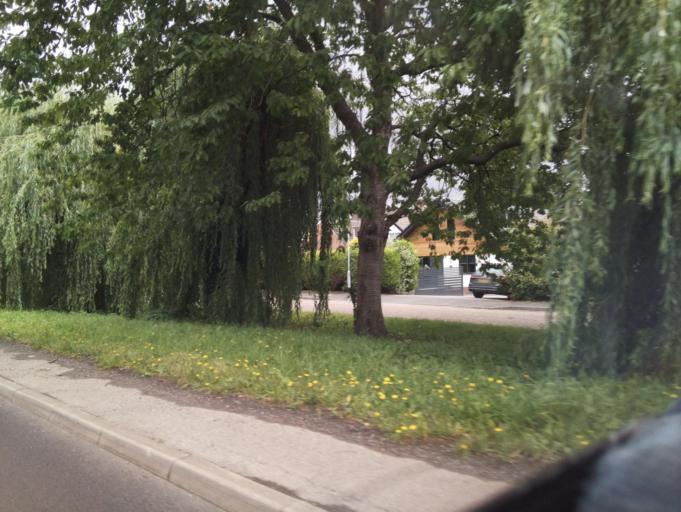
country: GB
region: England
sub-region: Nottinghamshire
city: Burton Joyce
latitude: 52.9933
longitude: -1.0267
